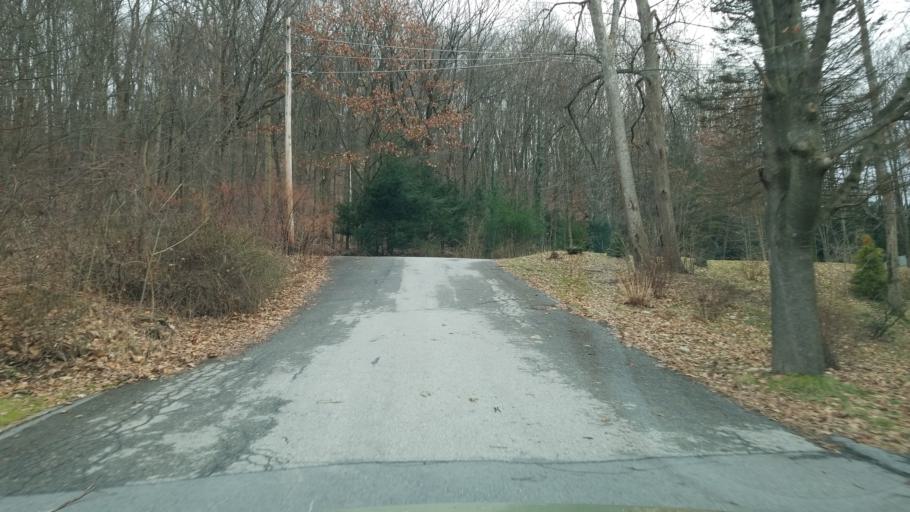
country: US
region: Pennsylvania
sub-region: Clearfield County
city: Clearfield
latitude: 41.0256
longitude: -78.4510
